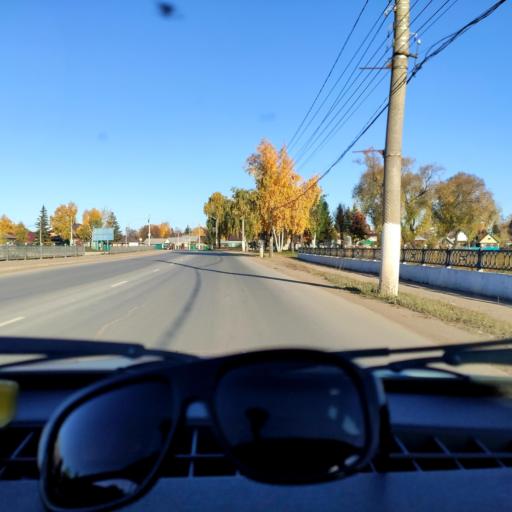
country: RU
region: Bashkortostan
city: Blagoveshchensk
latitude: 55.0331
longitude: 55.9676
